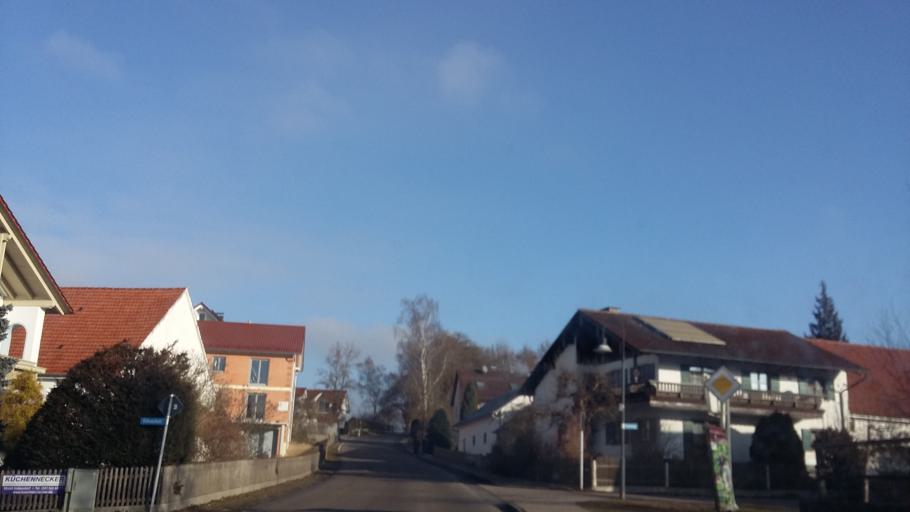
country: DE
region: Bavaria
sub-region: Swabia
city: Sielenbach
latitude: 48.3790
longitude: 11.1597
